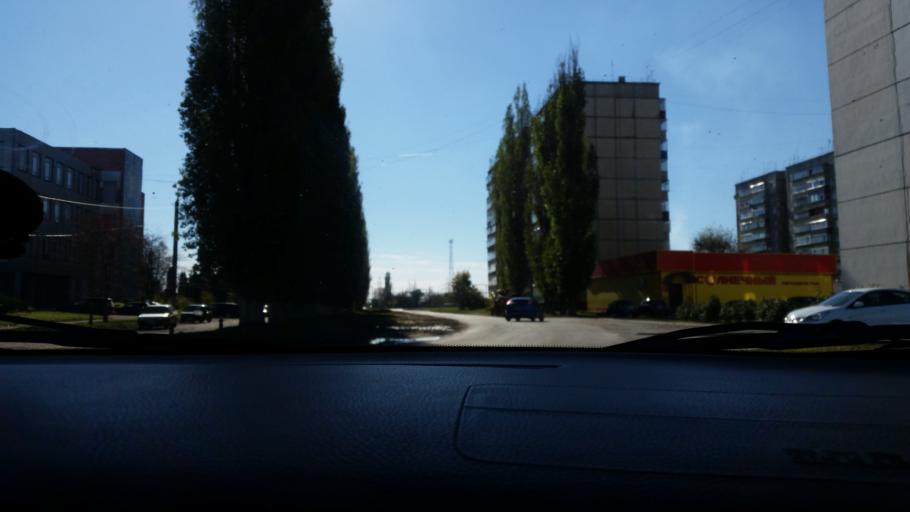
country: RU
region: Lipetsk
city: Gryazi
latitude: 52.4744
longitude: 39.9471
